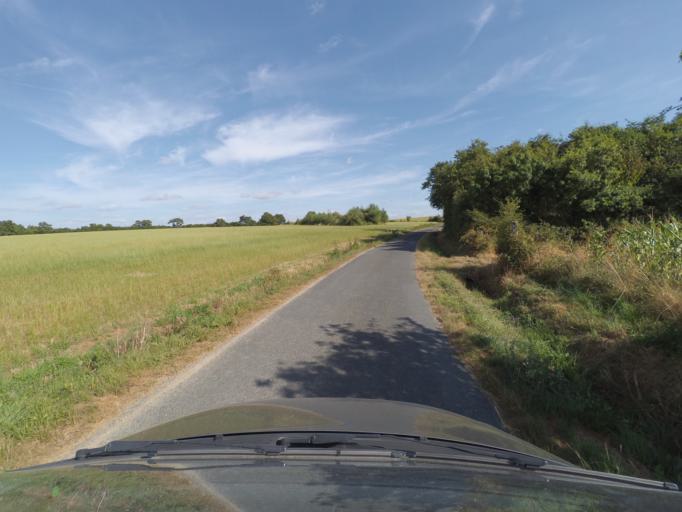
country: FR
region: Pays de la Loire
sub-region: Departement de la Loire-Atlantique
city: Le Bignon
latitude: 47.0907
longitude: -1.4644
